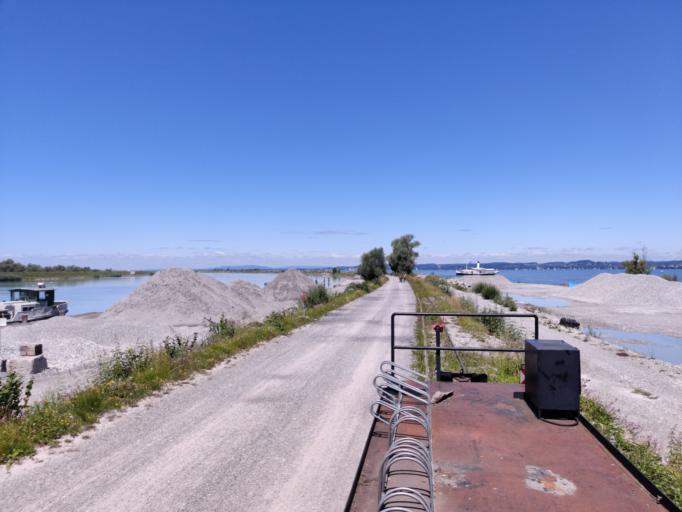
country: AT
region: Vorarlberg
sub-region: Politischer Bezirk Bregenz
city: Hard
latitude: 47.5035
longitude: 9.6711
